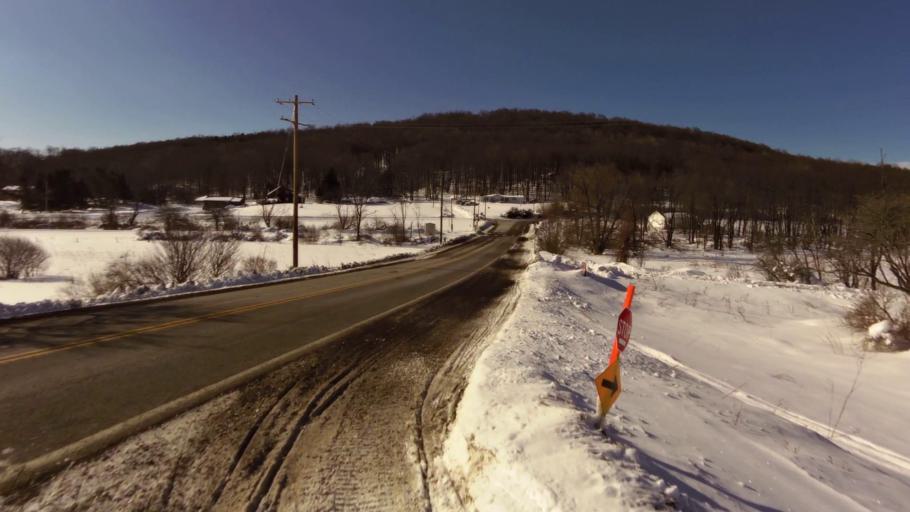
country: US
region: New York
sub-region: Cattaraugus County
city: Franklinville
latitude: 42.4059
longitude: -78.5044
